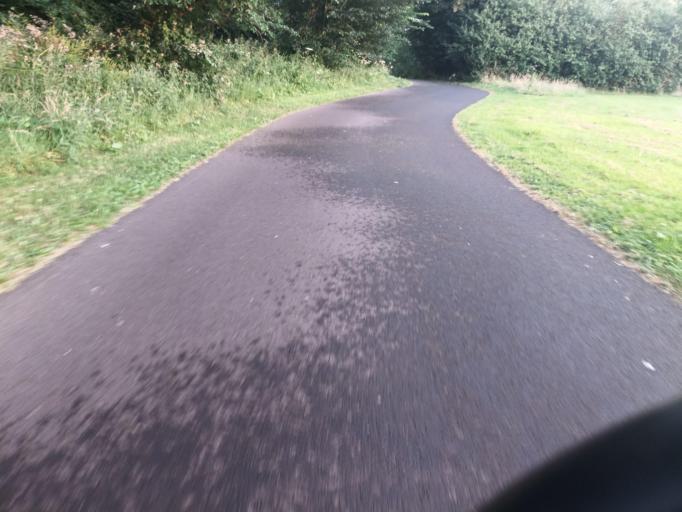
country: GB
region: Northern Ireland
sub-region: Castlereagh District
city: Dundonald
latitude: 54.5852
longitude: -5.7965
